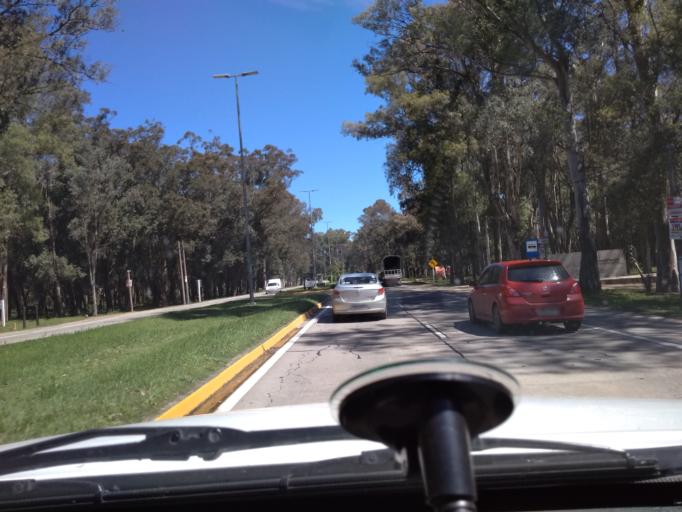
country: UY
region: Canelones
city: Barra de Carrasco
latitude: -34.8551
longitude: -56.0281
